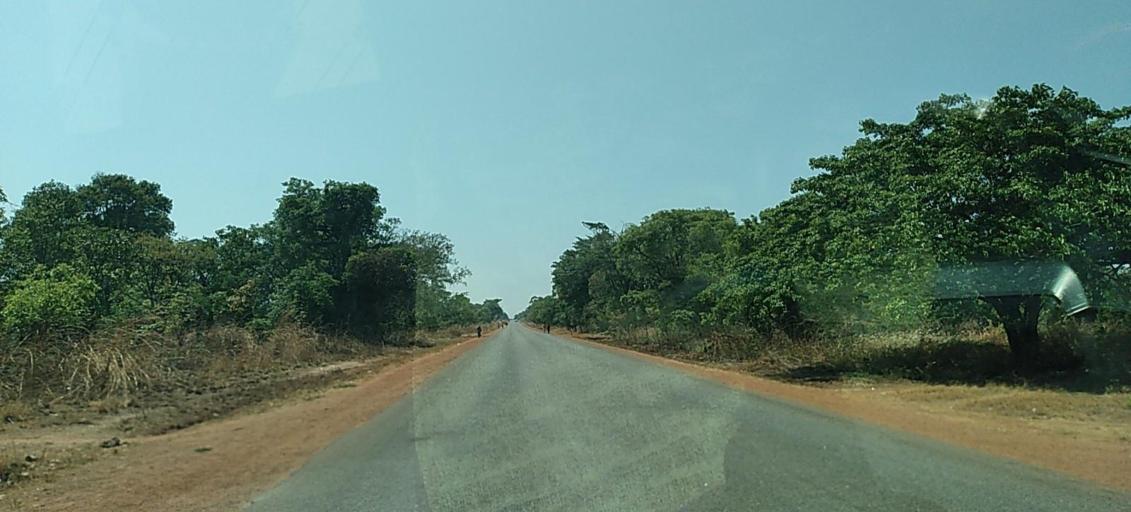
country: ZM
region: North-Western
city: Solwezi
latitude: -12.2812
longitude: 25.6851
